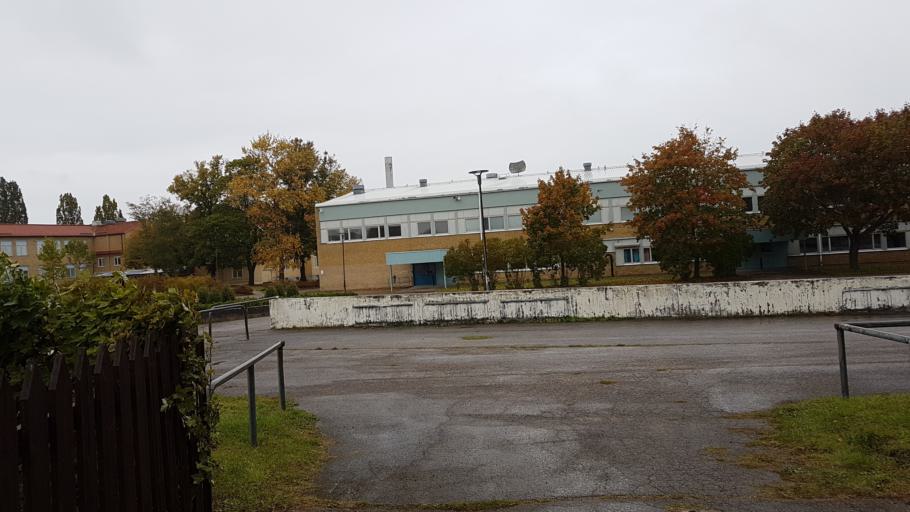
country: SE
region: Gotland
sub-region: Gotland
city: Visby
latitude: 57.6239
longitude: 18.2874
